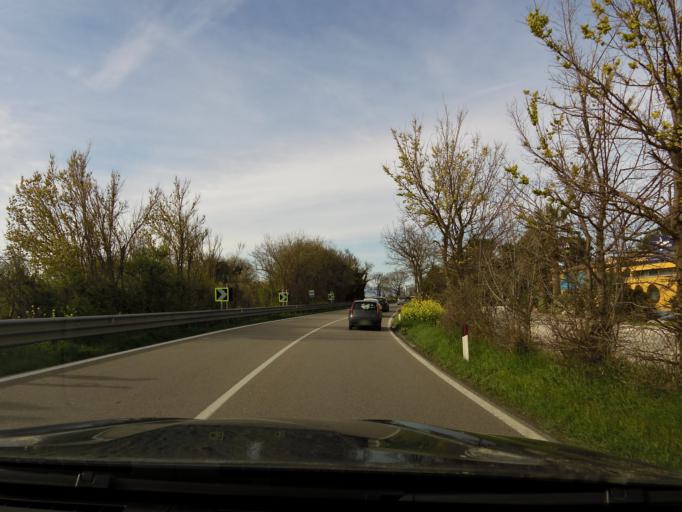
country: IT
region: The Marches
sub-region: Provincia di Macerata
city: Porto Potenza Picena
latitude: 43.3941
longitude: 13.6799
